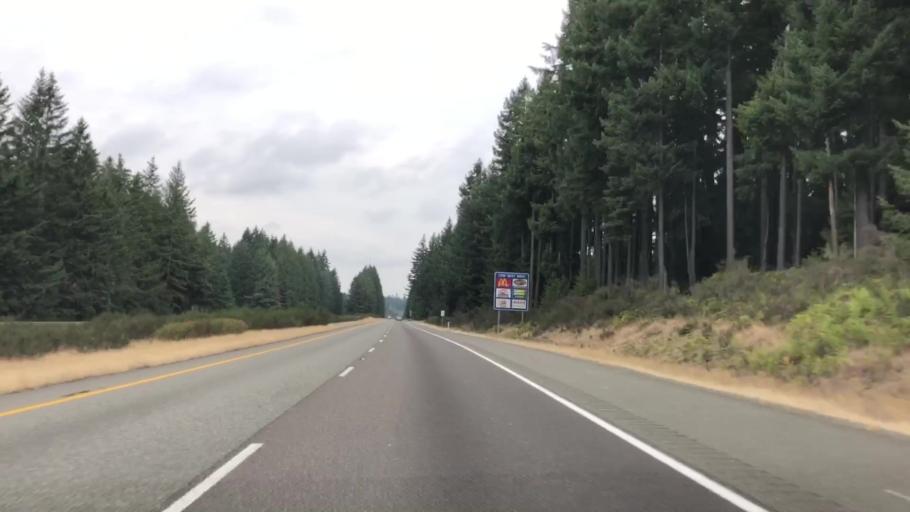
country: US
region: Washington
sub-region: Kitsap County
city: Bethel
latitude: 47.4912
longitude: -122.6357
